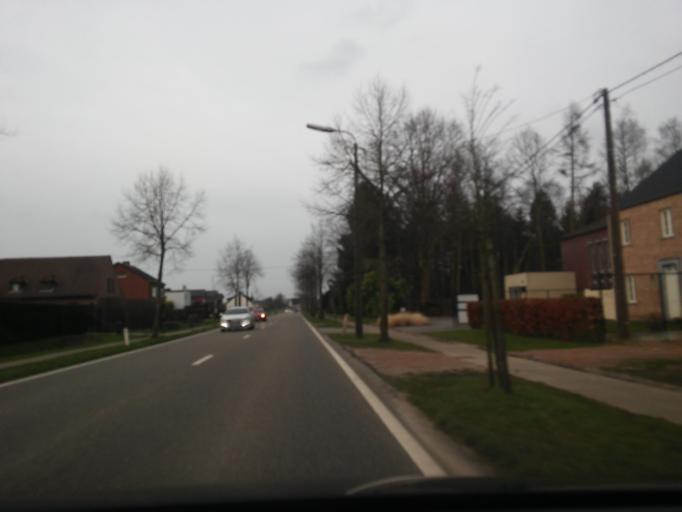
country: BE
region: Flanders
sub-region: Provincie Antwerpen
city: Herselt
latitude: 51.0778
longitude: 4.8762
